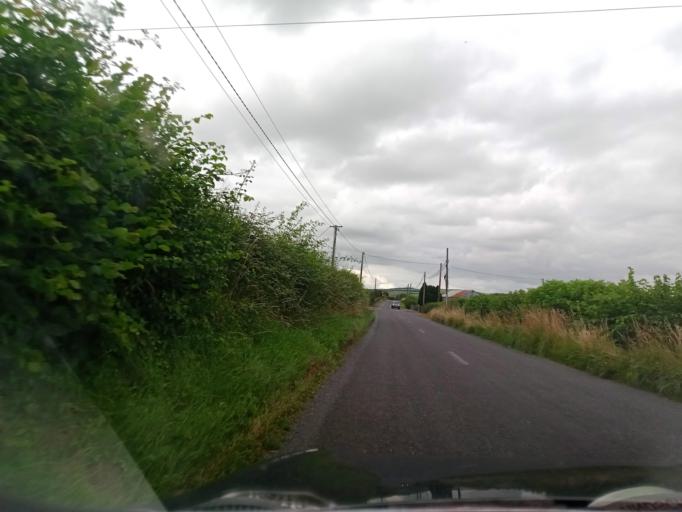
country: IE
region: Leinster
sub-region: Laois
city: Stradbally
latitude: 52.9695
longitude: -7.1847
